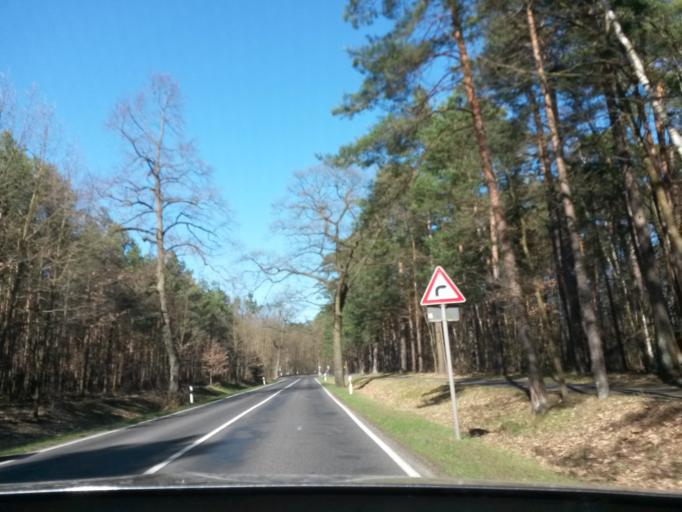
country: DE
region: Brandenburg
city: Grunheide
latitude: 52.4460
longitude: 13.8552
